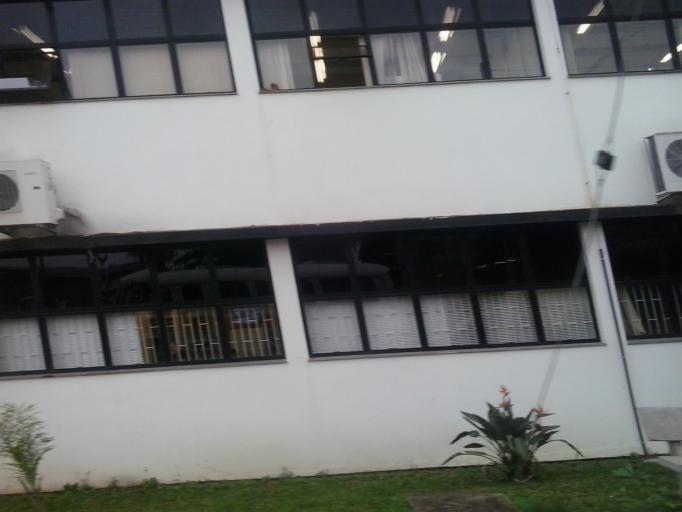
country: BR
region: Rio Grande do Sul
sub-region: Santa Maria
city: Santa Maria
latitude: -29.7120
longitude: -53.7183
